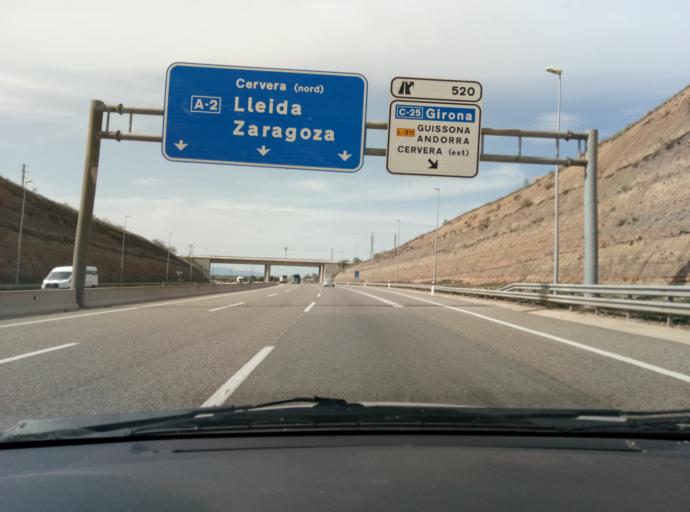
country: ES
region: Catalonia
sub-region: Provincia de Lleida
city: Cervera
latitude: 41.6758
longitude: 1.2902
